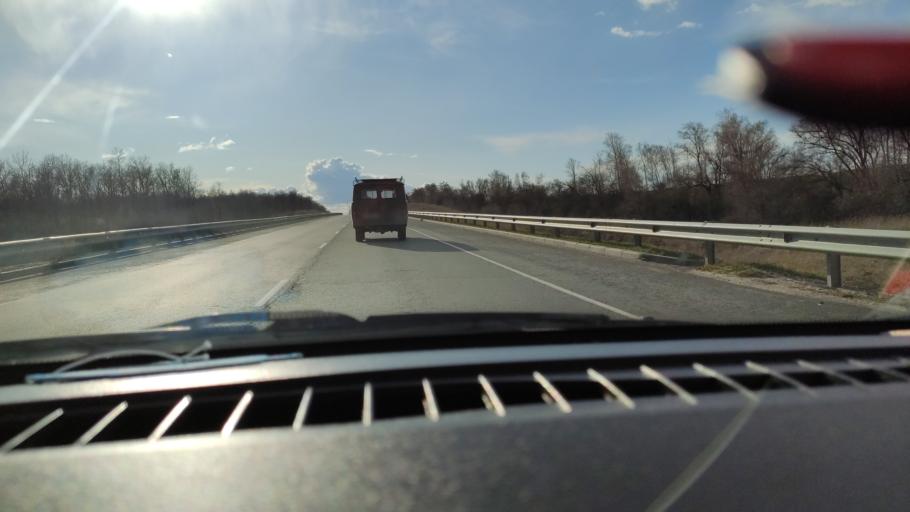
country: RU
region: Saratov
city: Yelshanka
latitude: 51.8242
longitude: 46.3057
